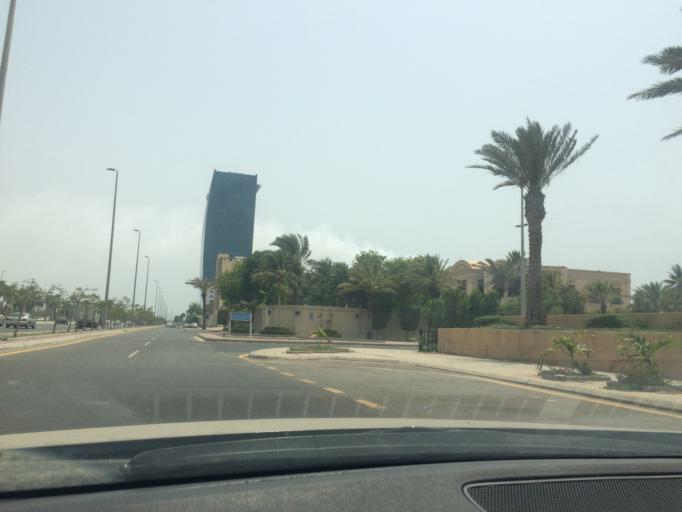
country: SA
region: Makkah
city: Jeddah
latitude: 21.5641
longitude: 39.1257
